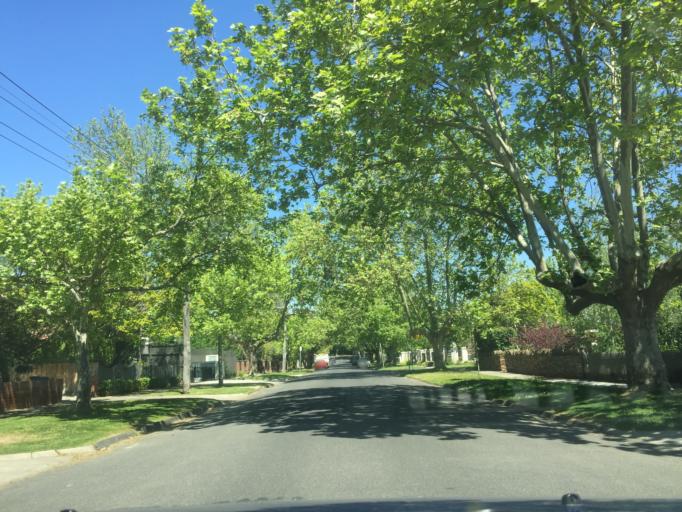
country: AU
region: Victoria
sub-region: Boroondara
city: Canterbury
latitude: -37.8212
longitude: 145.0846
